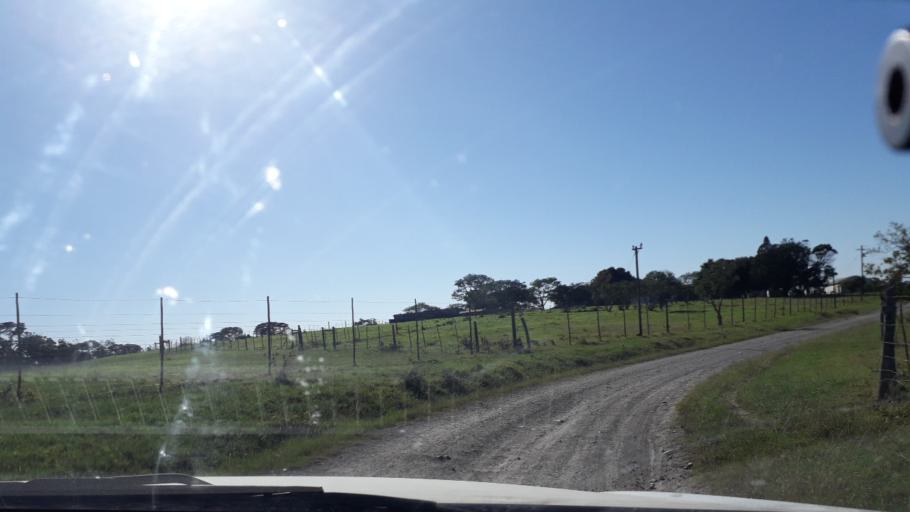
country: ZA
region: Eastern Cape
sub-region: Buffalo City Metropolitan Municipality
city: East London
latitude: -32.8415
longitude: 27.9741
